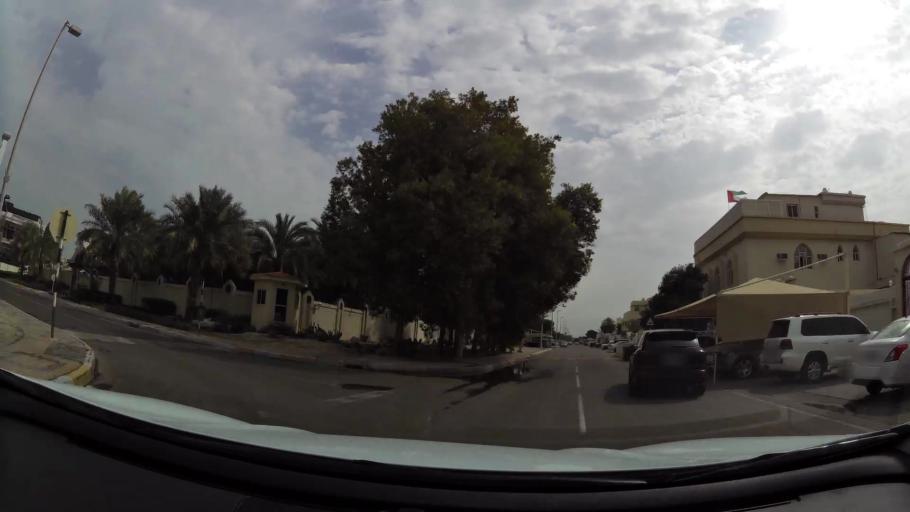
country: AE
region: Abu Dhabi
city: Abu Dhabi
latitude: 24.4433
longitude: 54.4328
